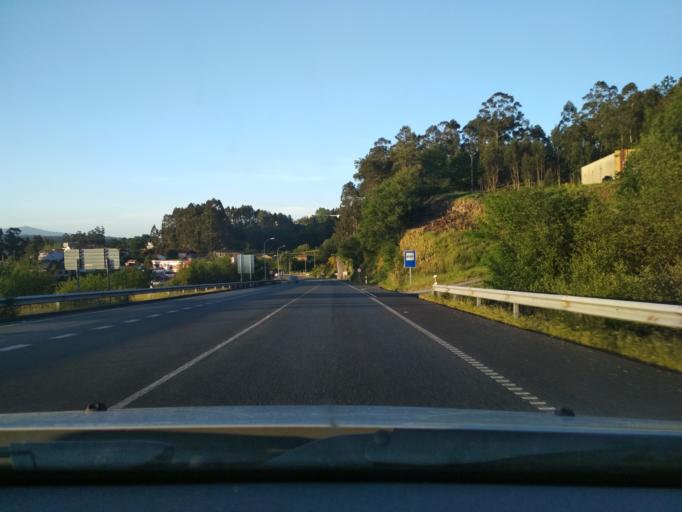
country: ES
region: Galicia
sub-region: Provincia de Pontevedra
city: Barro
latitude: 42.5176
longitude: -8.6399
